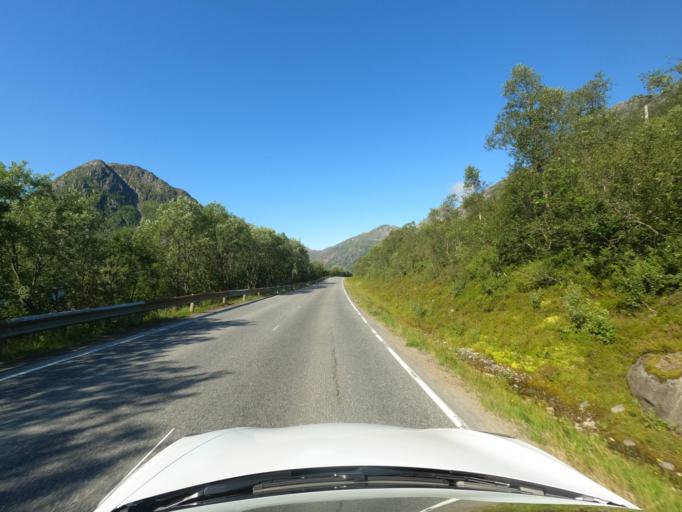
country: NO
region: Nordland
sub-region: Lodingen
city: Lodingen
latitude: 68.5592
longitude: 15.7703
